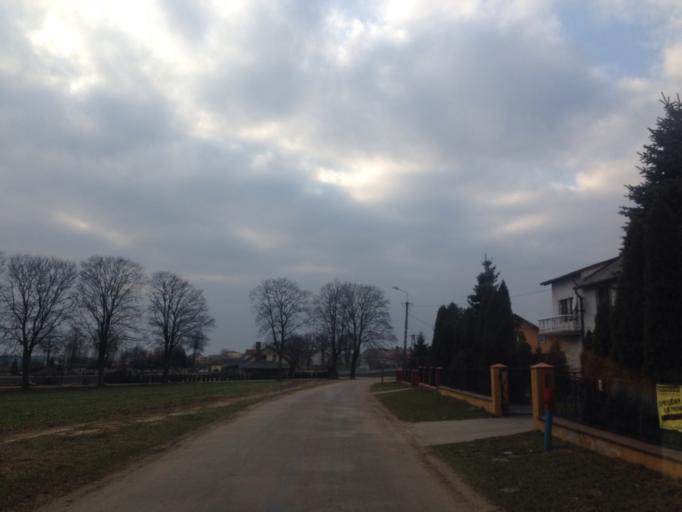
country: PL
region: Kujawsko-Pomorskie
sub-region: Powiat brodnicki
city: Brzozie
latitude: 53.3514
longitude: 19.7087
